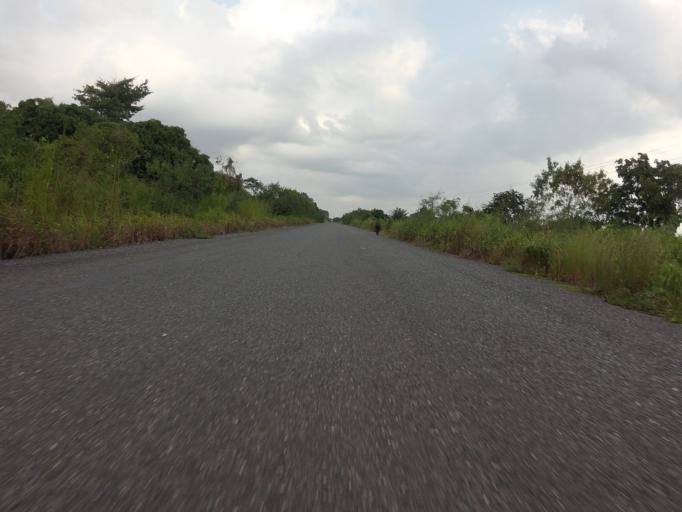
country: GH
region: Volta
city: Ho
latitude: 6.5008
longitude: 0.4874
